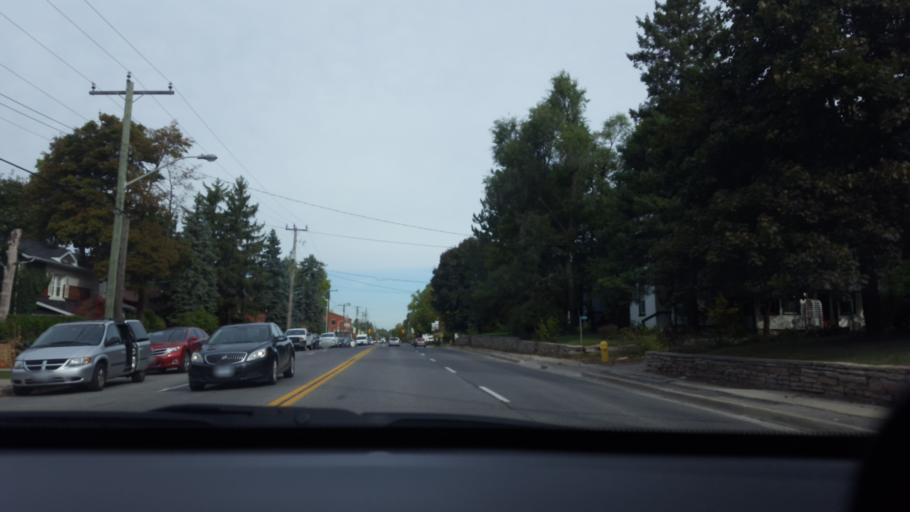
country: CA
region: Ontario
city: Vaughan
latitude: 43.9261
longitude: -79.5275
